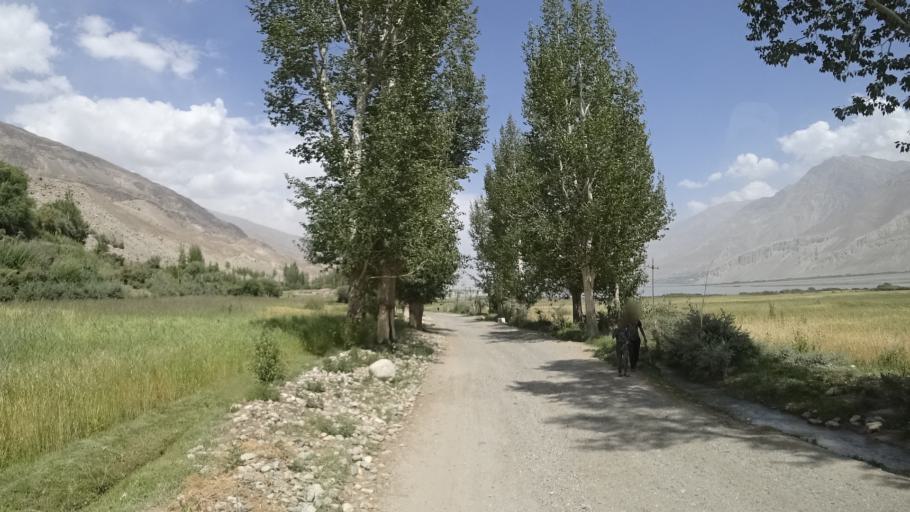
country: AF
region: Badakhshan
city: Khandud
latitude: 36.9255
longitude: 72.1989
